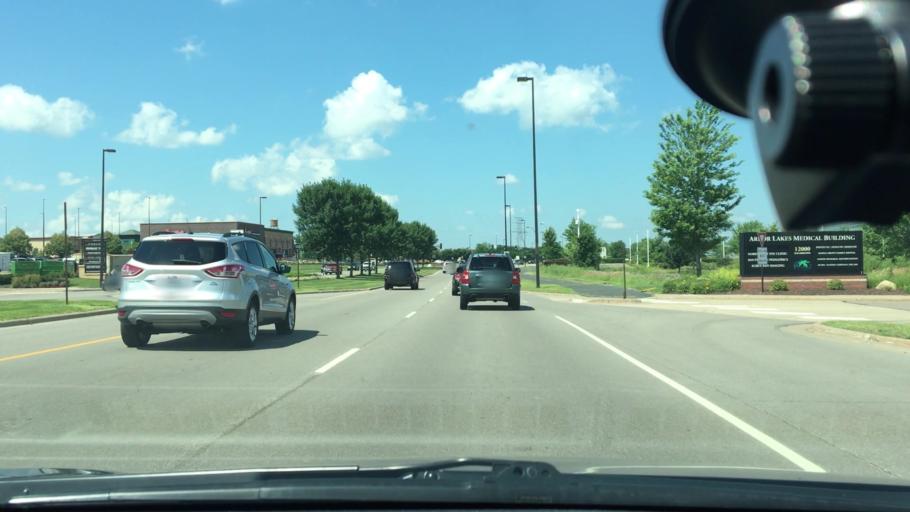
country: US
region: Minnesota
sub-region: Hennepin County
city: Maple Grove
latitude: 45.0947
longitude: -93.4338
